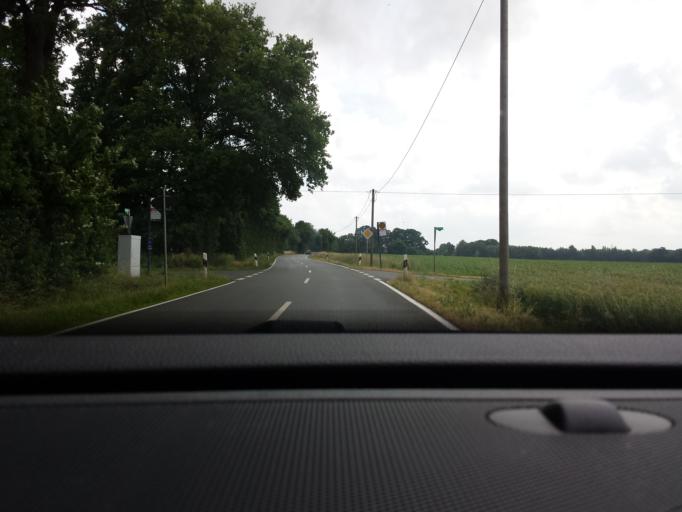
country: NL
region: Gelderland
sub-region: Berkelland
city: Eibergen
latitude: 52.0594
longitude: 6.7052
